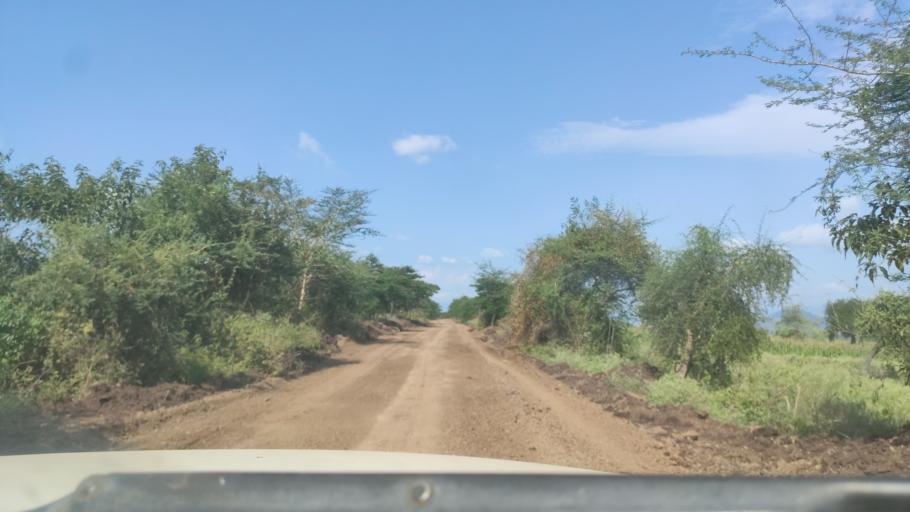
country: ET
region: Southern Nations, Nationalities, and People's Region
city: Felege Neway
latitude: 6.3797
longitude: 37.0906
